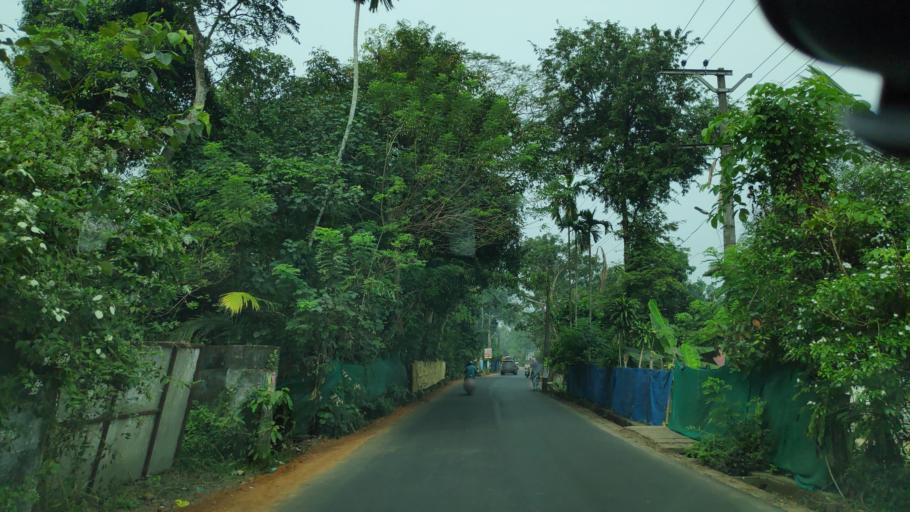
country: IN
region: Kerala
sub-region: Alappuzha
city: Alleppey
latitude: 9.5722
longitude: 76.3448
